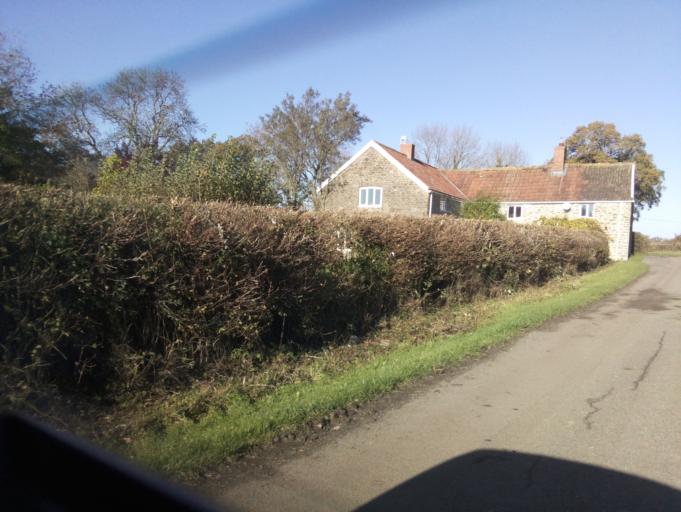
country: GB
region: England
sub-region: Somerset
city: Yeovil
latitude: 50.8827
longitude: -2.5948
